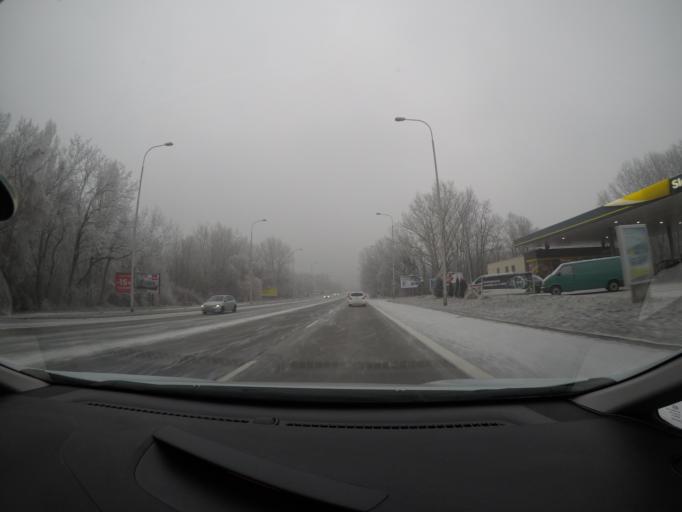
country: SK
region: Bratislavsky
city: Bratislava
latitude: 48.1063
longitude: 17.1234
